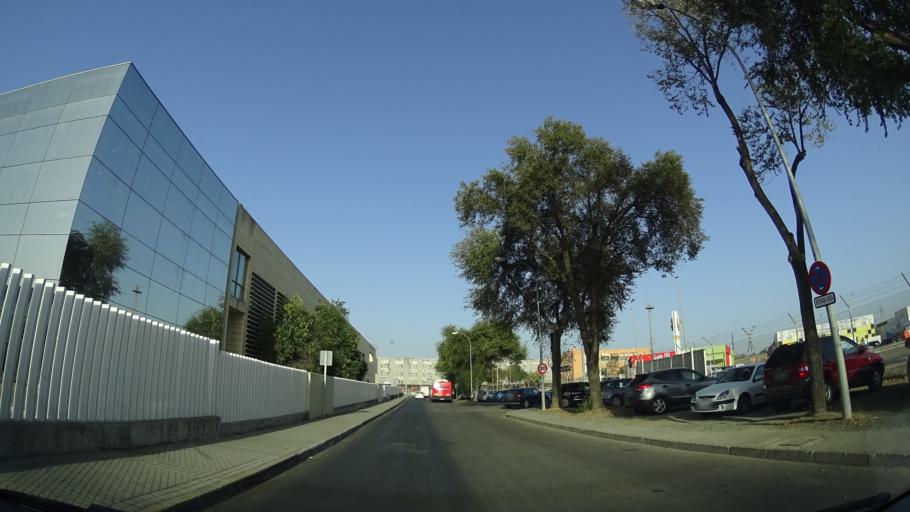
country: ES
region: Andalusia
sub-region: Provincia de Sevilla
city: La Algaba
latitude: 37.4312
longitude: -5.9785
